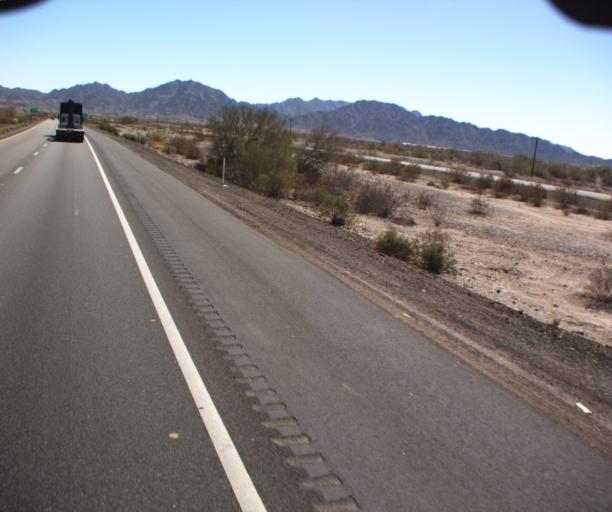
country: US
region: Arizona
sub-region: Yuma County
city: Fortuna Foothills
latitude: 32.6646
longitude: -114.3891
